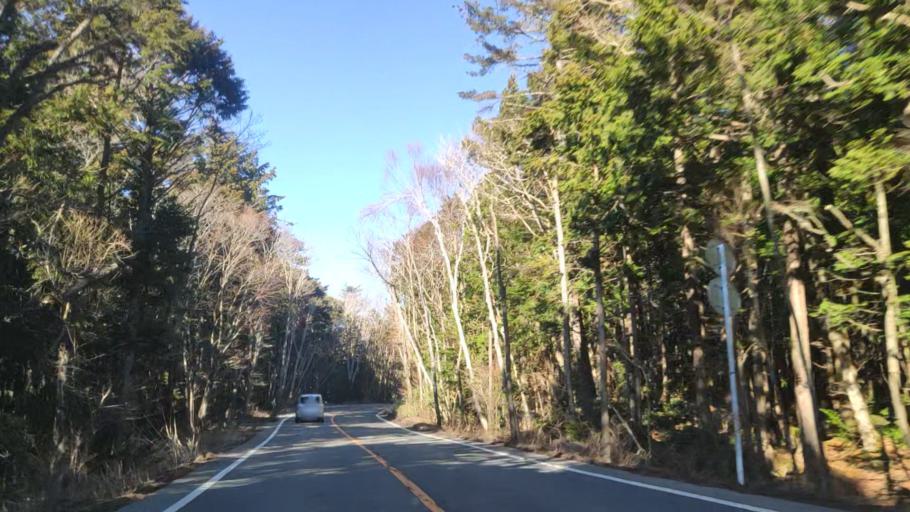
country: JP
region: Yamanashi
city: Fujikawaguchiko
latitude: 35.4585
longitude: 138.6533
